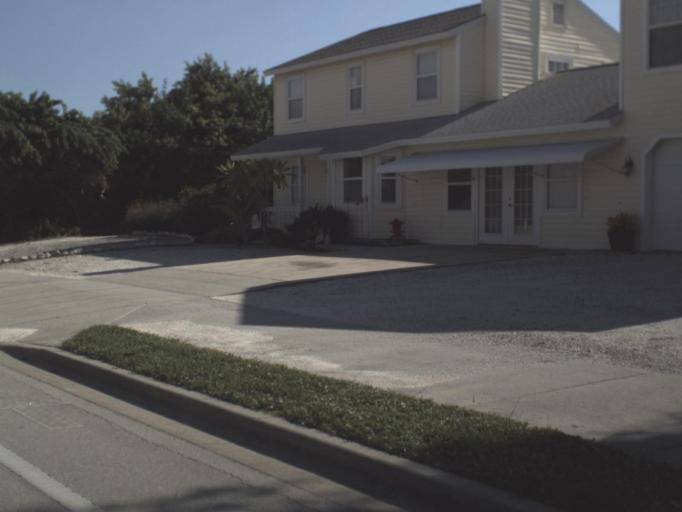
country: US
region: Florida
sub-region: Sarasota County
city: South Venice
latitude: 27.0449
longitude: -82.4031
